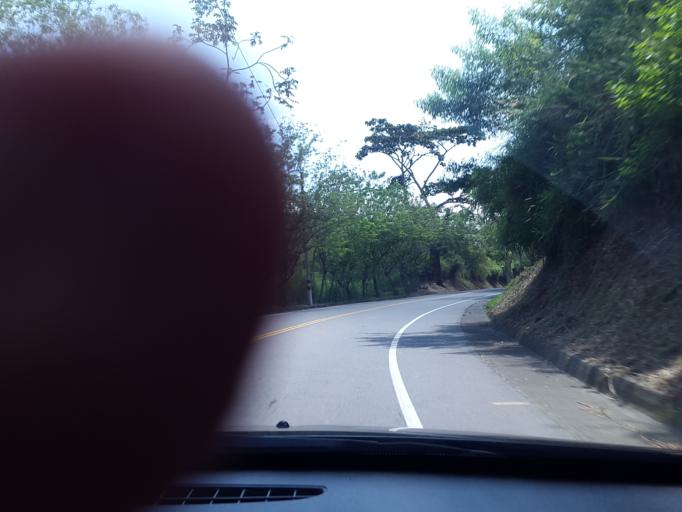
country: CO
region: Valle del Cauca
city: Alcala
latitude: 4.6968
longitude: -75.8279
